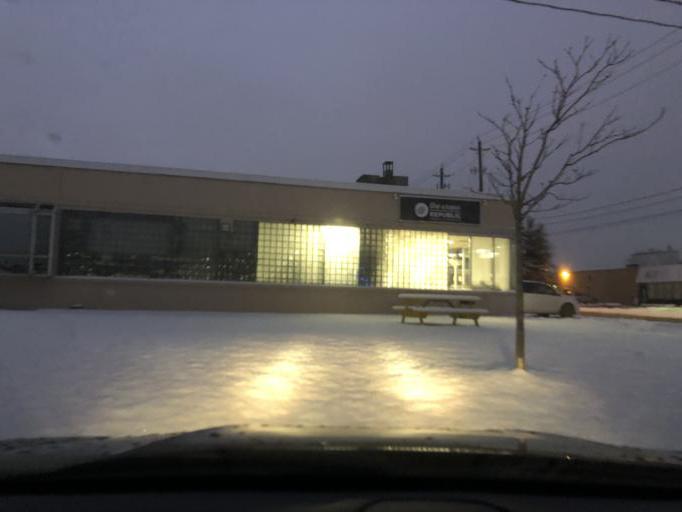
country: CA
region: Ontario
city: Toronto
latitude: 43.7050
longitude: -79.4709
